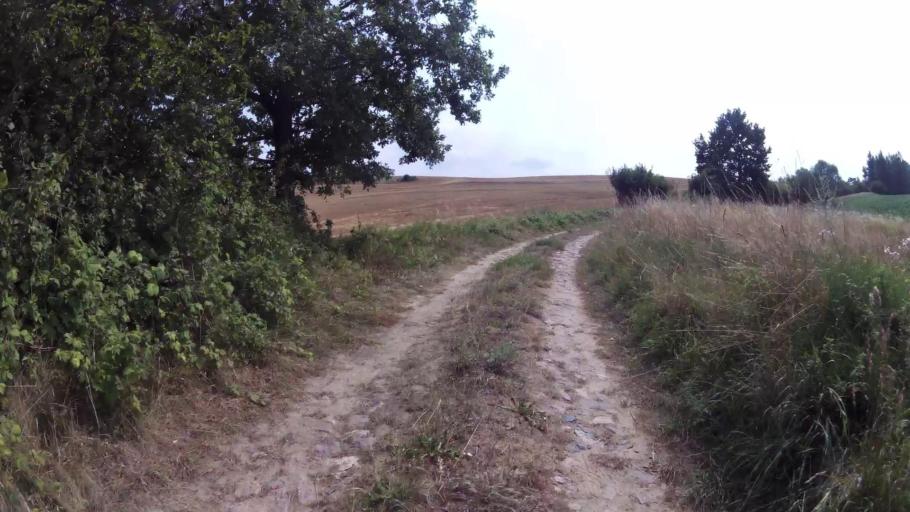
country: PL
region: West Pomeranian Voivodeship
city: Trzcinsko Zdroj
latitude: 52.9008
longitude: 14.5216
